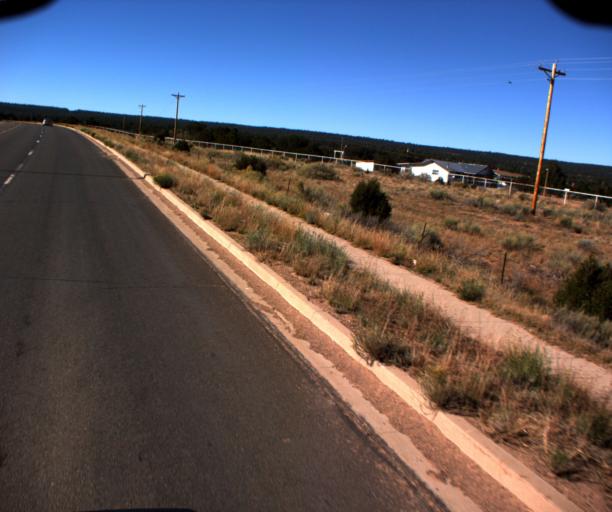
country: US
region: Arizona
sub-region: Apache County
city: Saint Michaels
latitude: 35.6589
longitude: -109.1153
